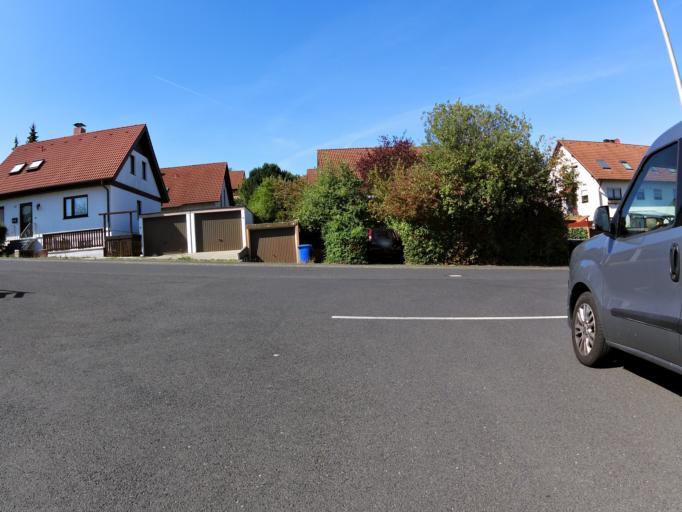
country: DE
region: Bavaria
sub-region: Regierungsbezirk Unterfranken
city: Margetshochheim
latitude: 49.8415
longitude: 9.8584
